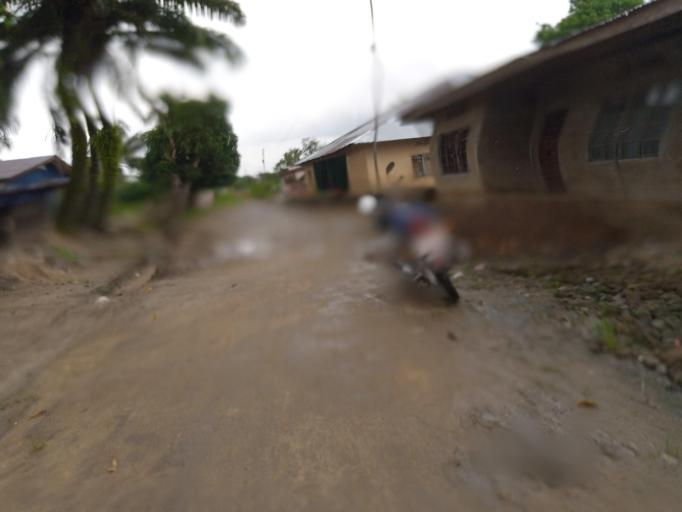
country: SL
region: Eastern Province
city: Kenema
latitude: 7.8559
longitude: -11.2001
